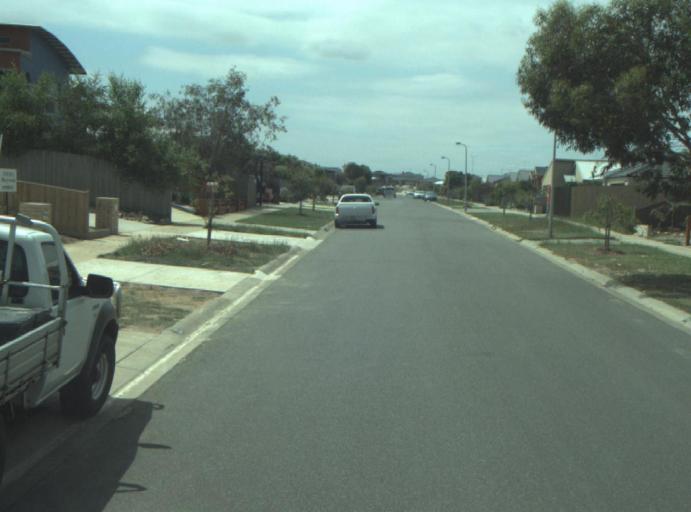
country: AU
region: Victoria
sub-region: Greater Geelong
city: Clifton Springs
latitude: -38.2554
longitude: 144.5517
